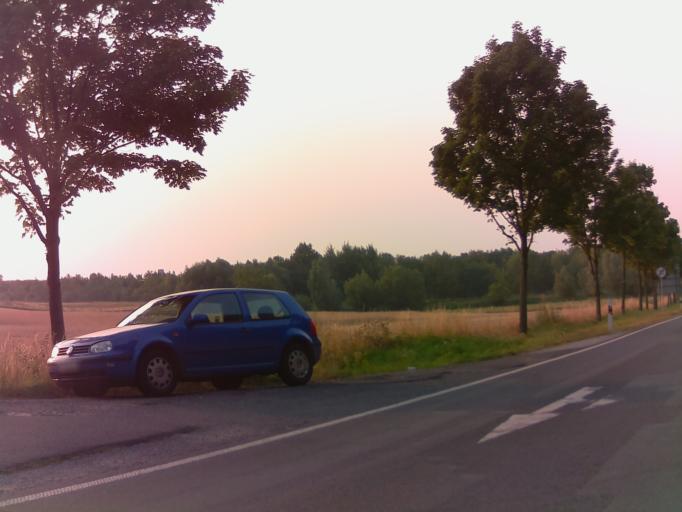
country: DE
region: Thuringia
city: Nohra
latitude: 50.9511
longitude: 11.2415
